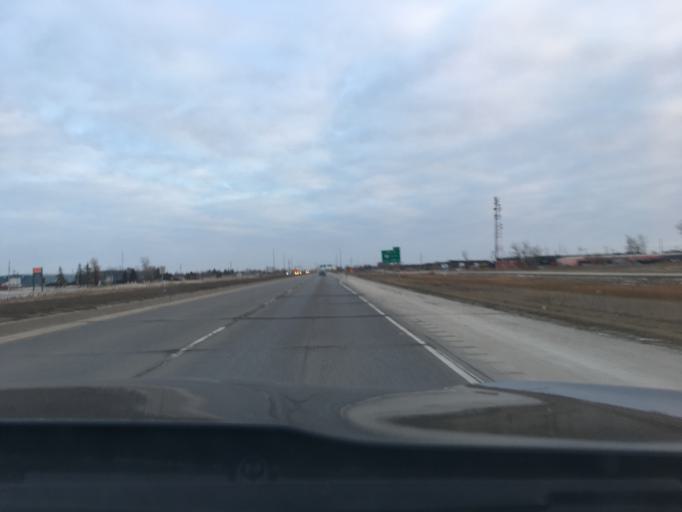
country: CA
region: Manitoba
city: Winnipeg
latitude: 49.9779
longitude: -97.0871
